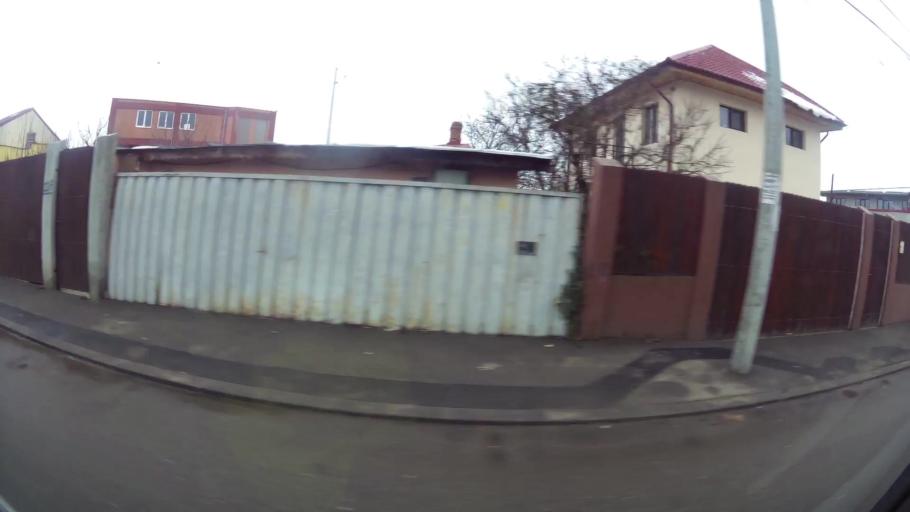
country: RO
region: Ilfov
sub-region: Comuna Popesti-Leordeni
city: Popesti-Leordeni
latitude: 44.4070
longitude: 26.1695
